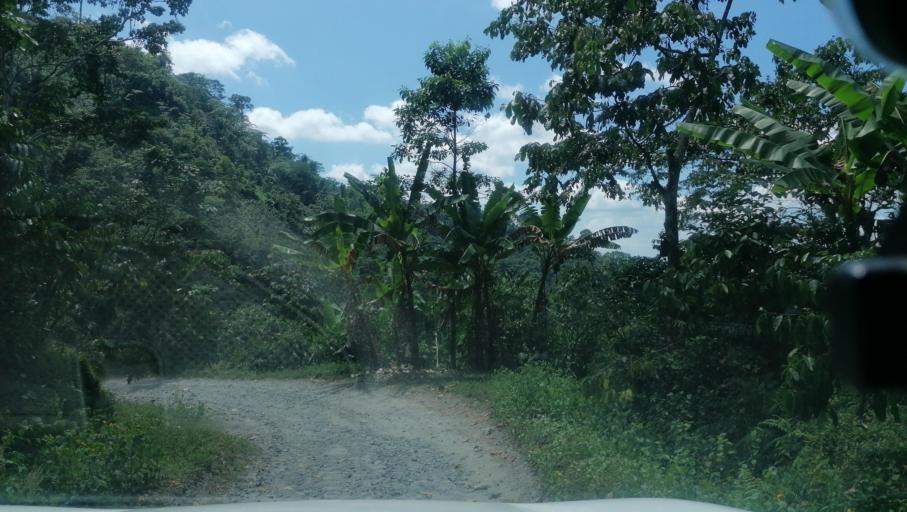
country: MX
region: Chiapas
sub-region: Union Juarez
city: Santo Domingo
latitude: 15.0729
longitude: -92.1313
